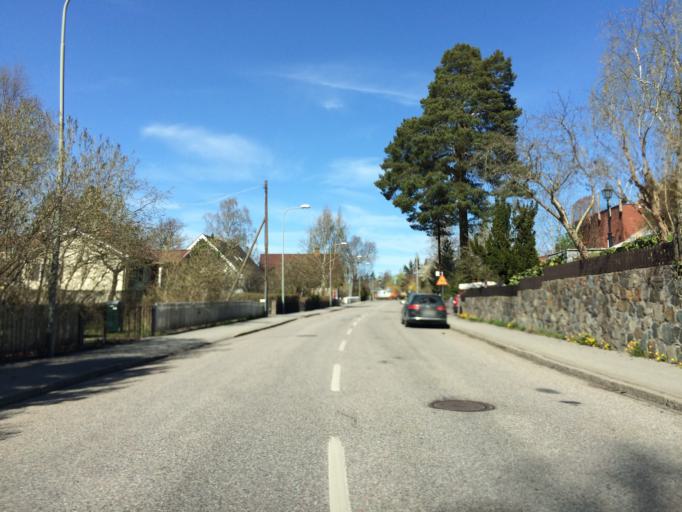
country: SE
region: Stockholm
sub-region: Huddinge Kommun
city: Huddinge
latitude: 59.2706
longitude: 17.9683
